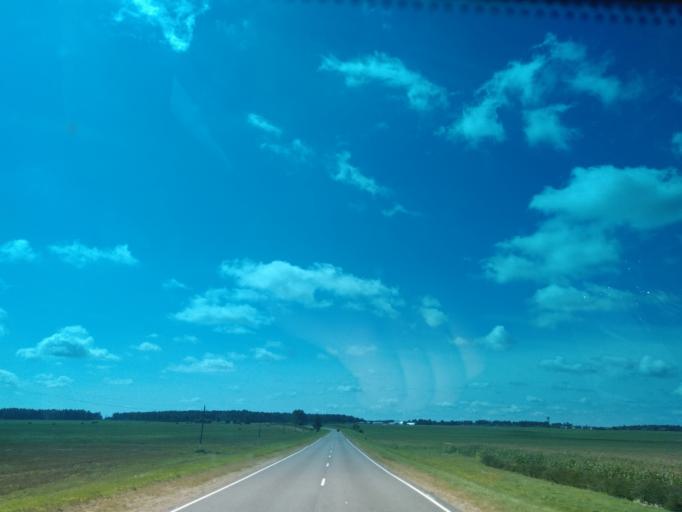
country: BY
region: Minsk
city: Uzda
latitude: 53.3666
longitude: 27.2302
